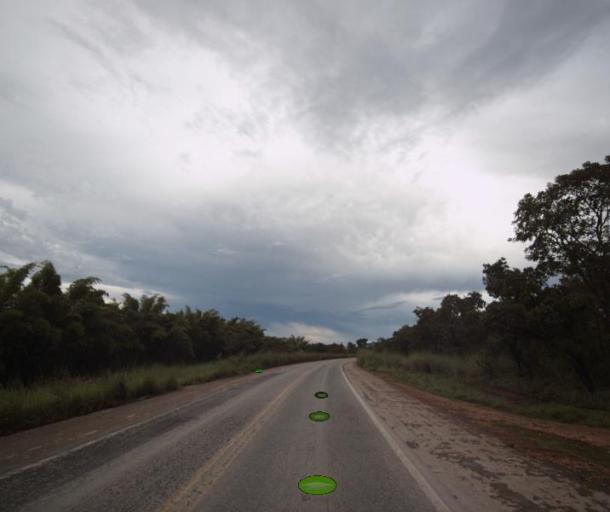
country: BR
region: Goias
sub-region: Porangatu
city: Porangatu
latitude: -13.5575
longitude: -49.0625
